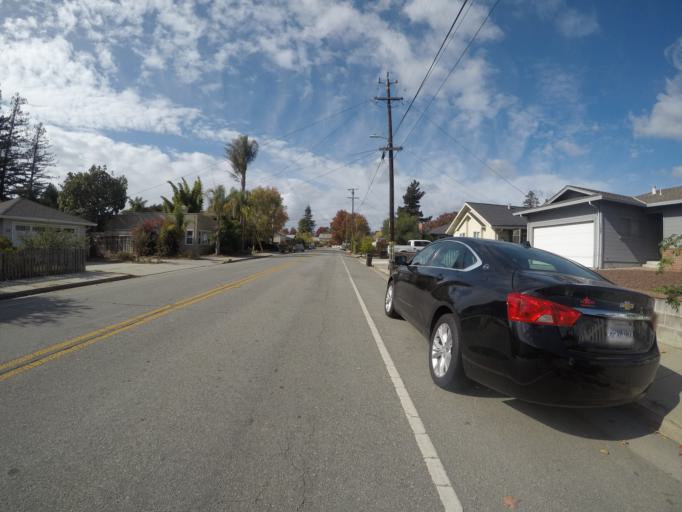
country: US
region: California
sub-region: Santa Cruz County
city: Pasatiempo
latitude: 36.9878
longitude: -122.0098
